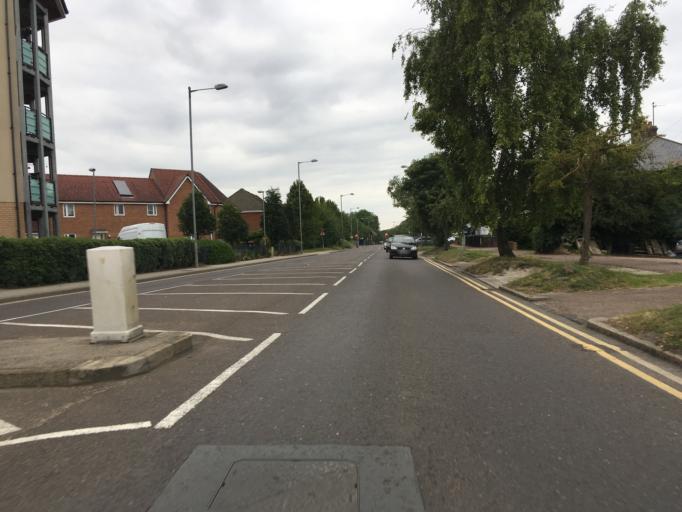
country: GB
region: England
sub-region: Central Bedfordshire
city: Dunstable
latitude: 51.8957
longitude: -0.5346
